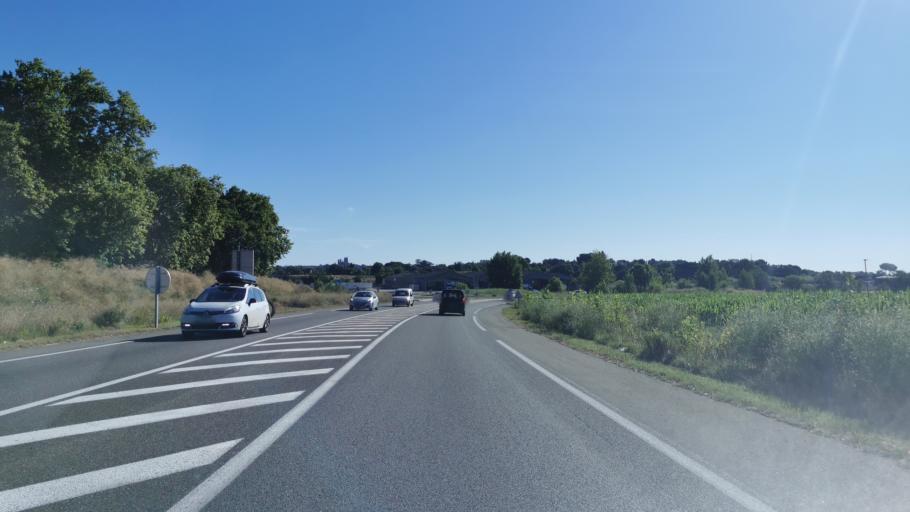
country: FR
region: Languedoc-Roussillon
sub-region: Departement de l'Herault
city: Beziers
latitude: 43.3221
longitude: 3.1877
